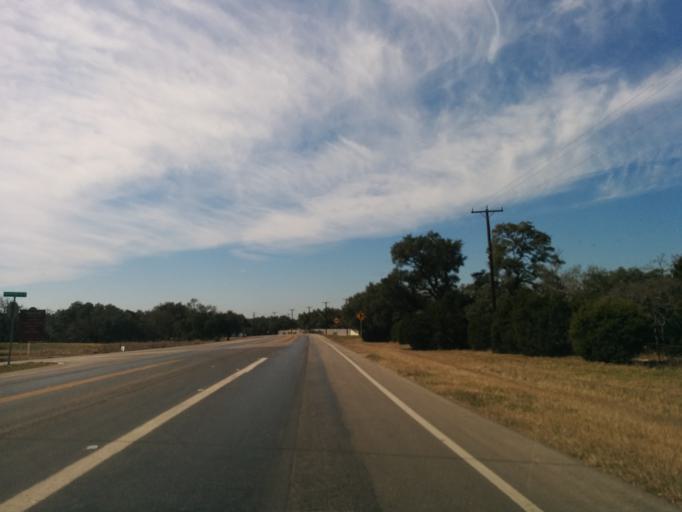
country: US
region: Texas
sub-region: Bexar County
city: Fair Oaks Ranch
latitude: 29.7560
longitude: -98.6196
